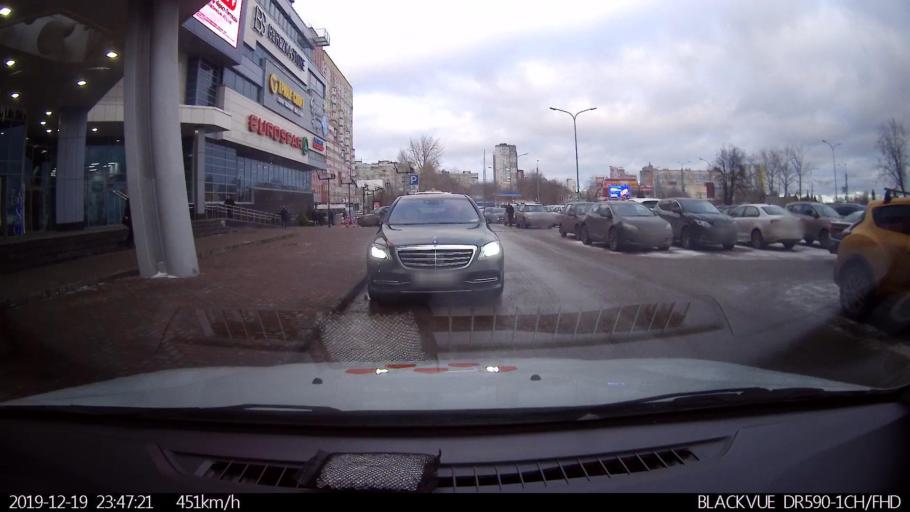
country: RU
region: Jaroslavl
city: Borok
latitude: 58.2074
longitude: 38.3868
